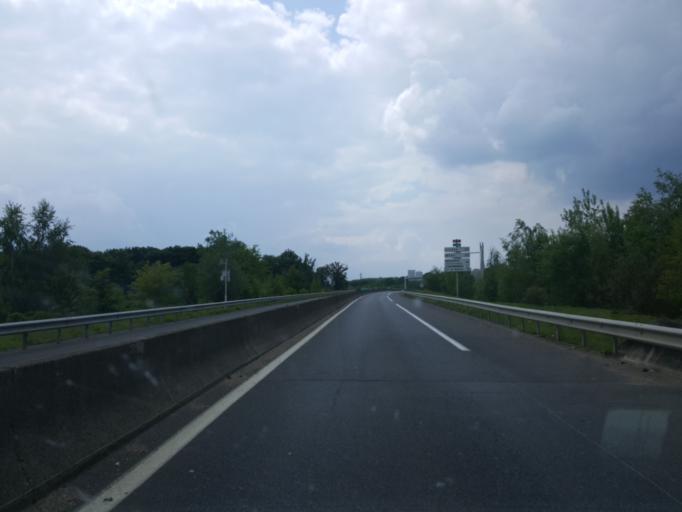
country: FR
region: Picardie
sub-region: Departement de l'Oise
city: Allonne
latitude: 49.3982
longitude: 2.1267
